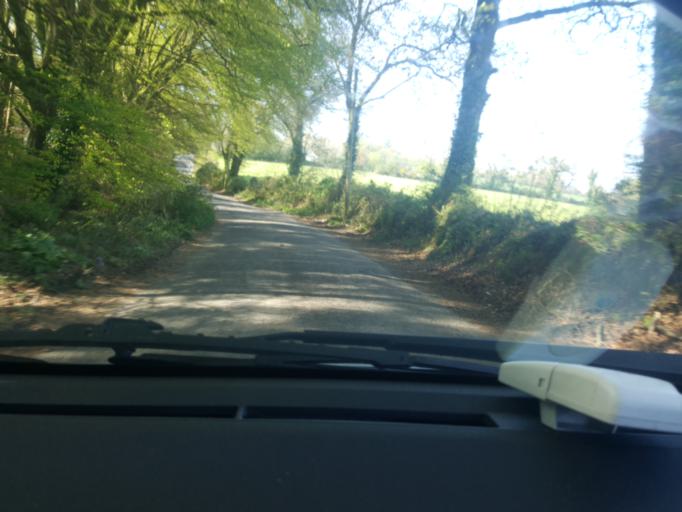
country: IE
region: Munster
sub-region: County Cork
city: Bandon
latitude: 51.7687
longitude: -8.6845
